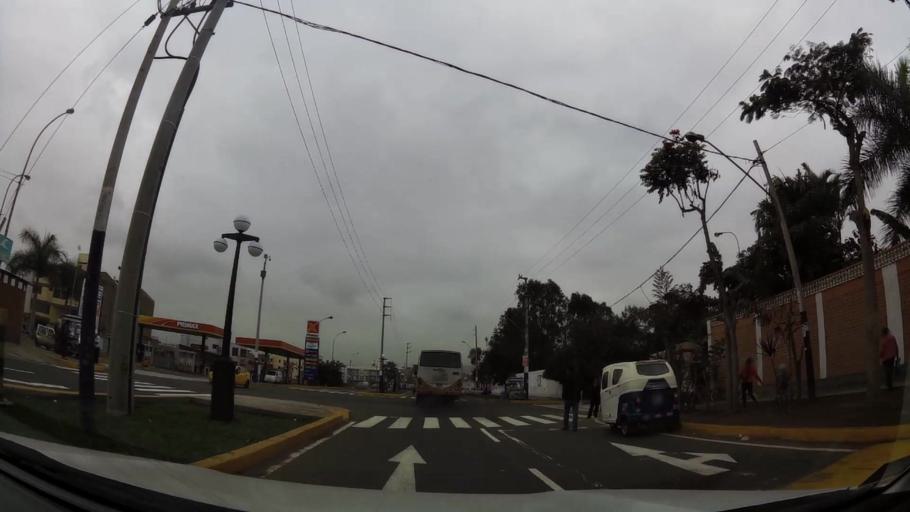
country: PE
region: Lima
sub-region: Lima
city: Surco
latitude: -12.2066
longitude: -77.0111
